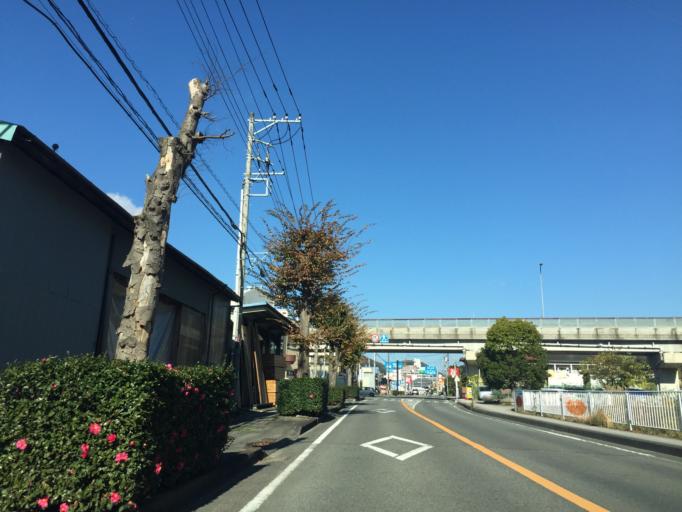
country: JP
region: Shizuoka
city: Mishima
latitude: 35.0250
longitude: 138.9298
